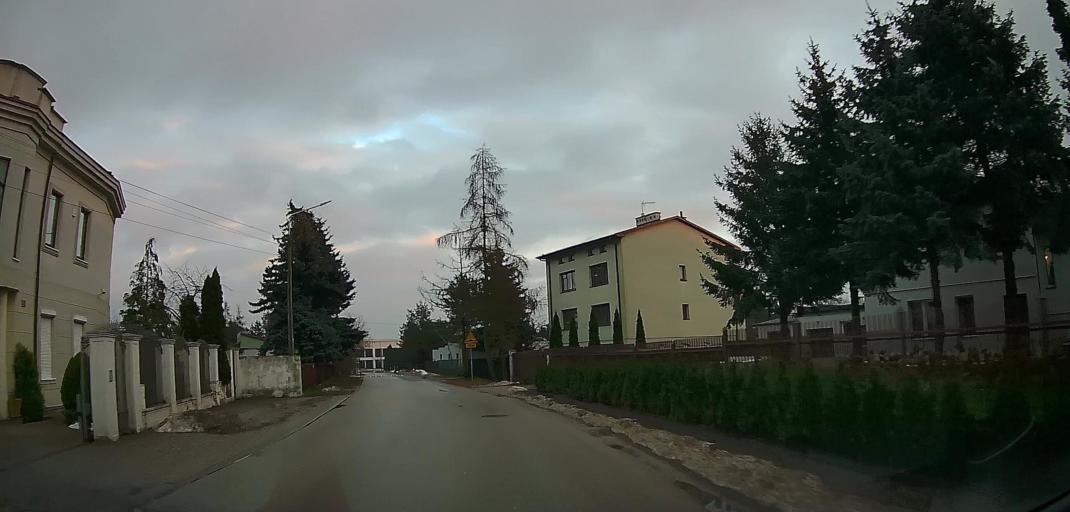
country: PL
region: Masovian Voivodeship
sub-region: Radom
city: Radom
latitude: 51.4475
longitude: 21.1413
